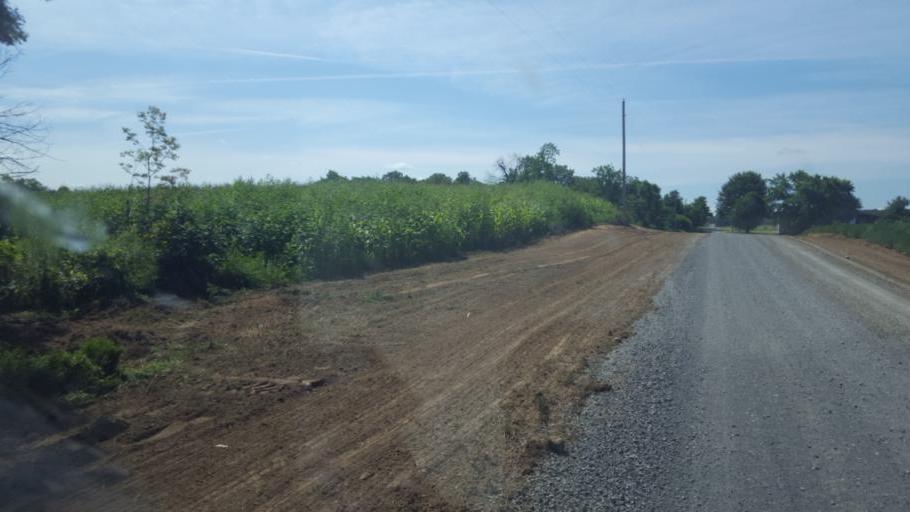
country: US
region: Ohio
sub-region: Knox County
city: Centerburg
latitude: 40.4442
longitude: -82.7172
